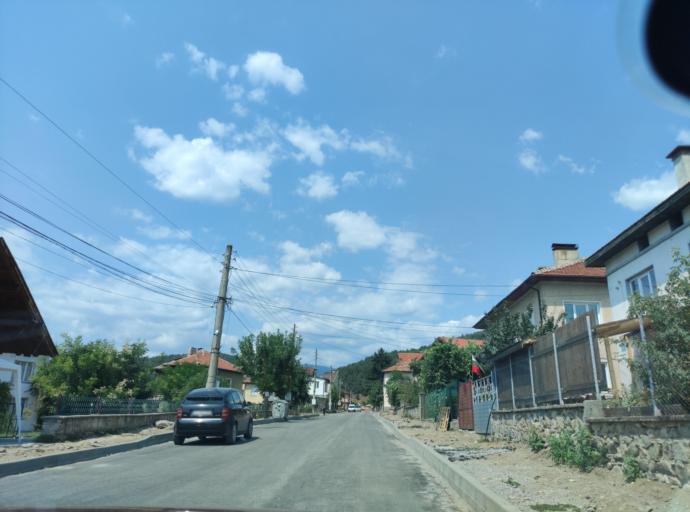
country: BG
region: Blagoevgrad
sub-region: Obshtina Belitsa
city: Belitsa
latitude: 41.9465
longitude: 23.5638
